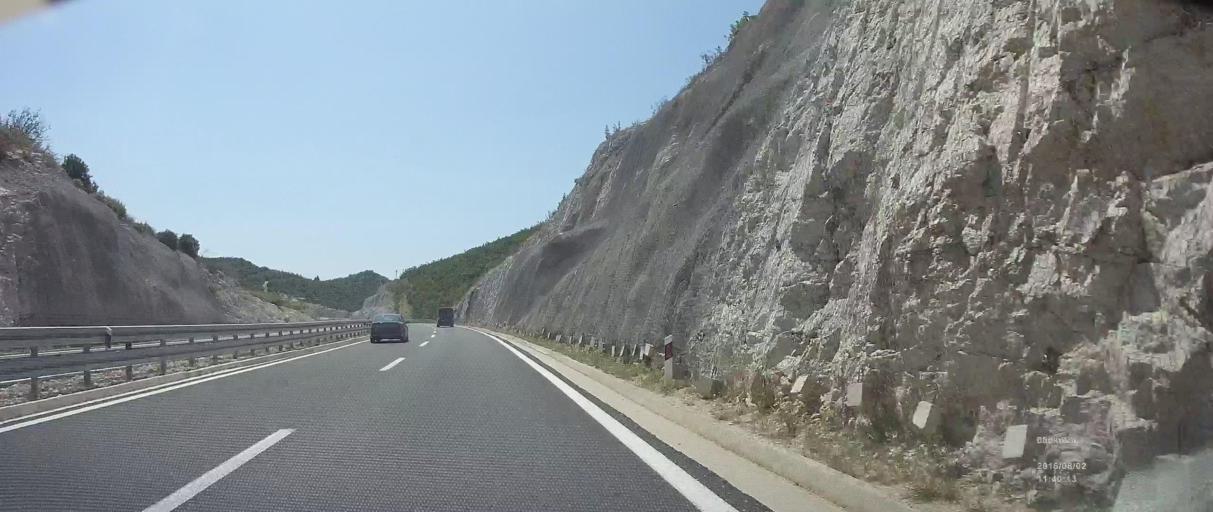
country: HR
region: Dubrovacko-Neretvanska
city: Komin
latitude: 43.0772
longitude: 17.4900
